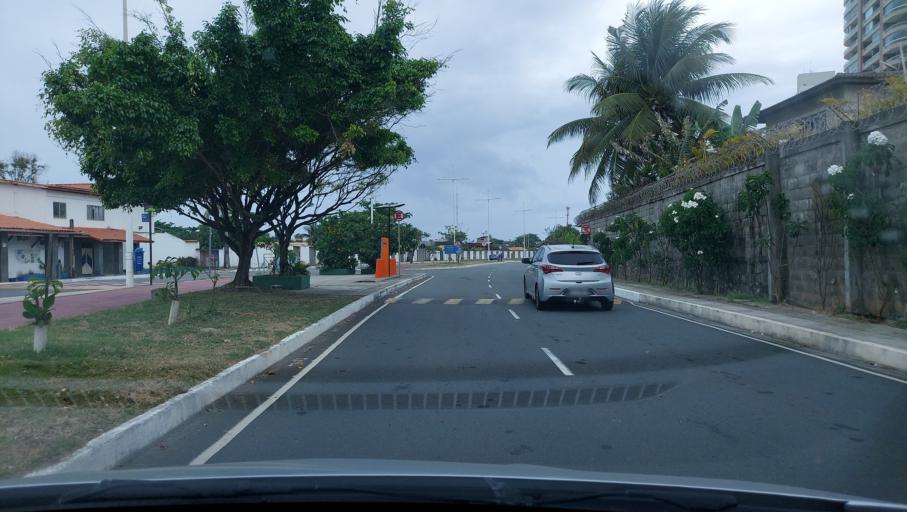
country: BR
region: Bahia
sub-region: Lauro De Freitas
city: Lauro de Freitas
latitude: -12.9591
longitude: -38.4018
